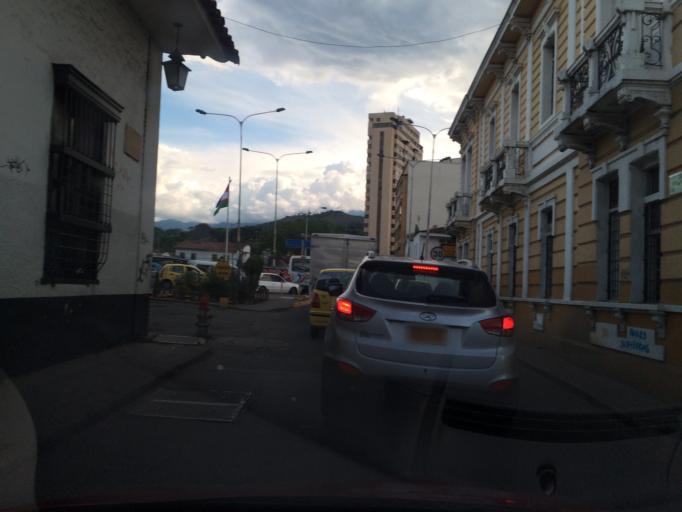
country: CO
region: Valle del Cauca
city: Cali
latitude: 3.4499
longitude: -76.5372
